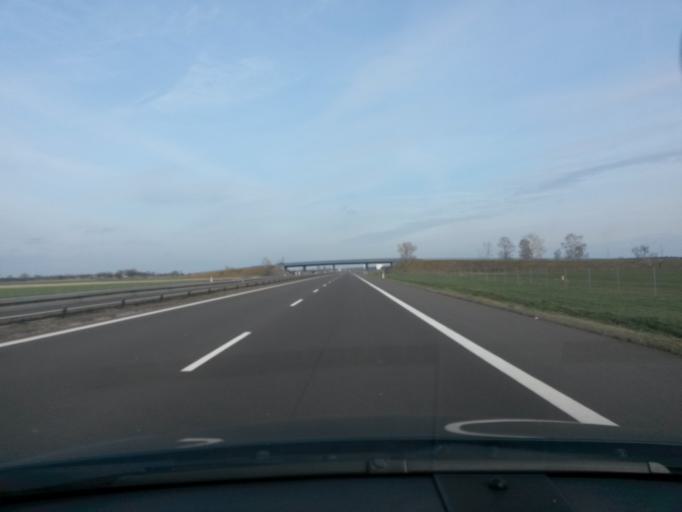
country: PL
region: Greater Poland Voivodeship
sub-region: Powiat sredzki
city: Dominowo
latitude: 52.3100
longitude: 17.2976
